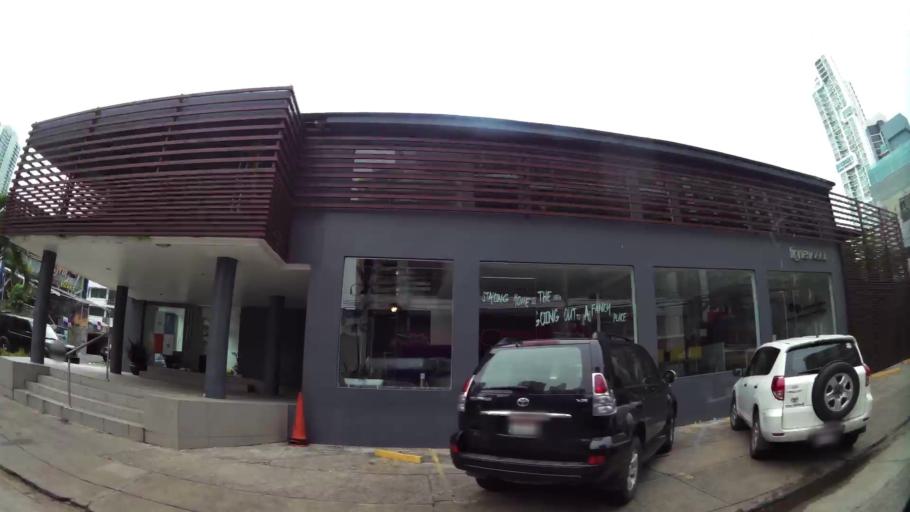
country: PA
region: Panama
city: Panama
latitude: 8.9787
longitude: -79.5256
